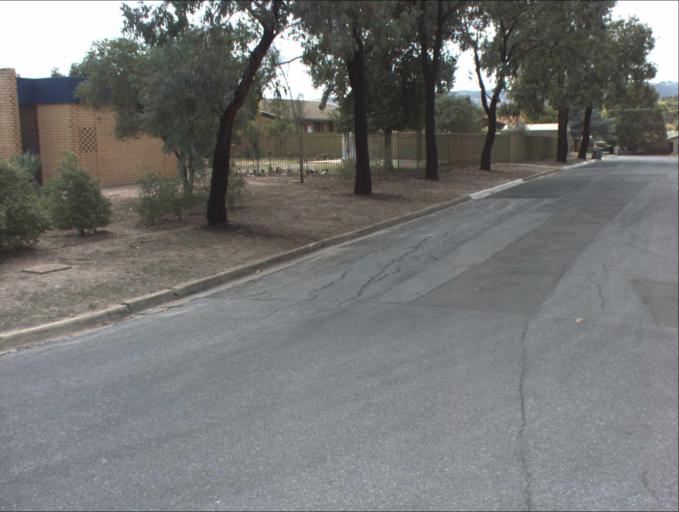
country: AU
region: South Australia
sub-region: Campbelltown
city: Paradise
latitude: -34.8589
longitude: 138.6684
